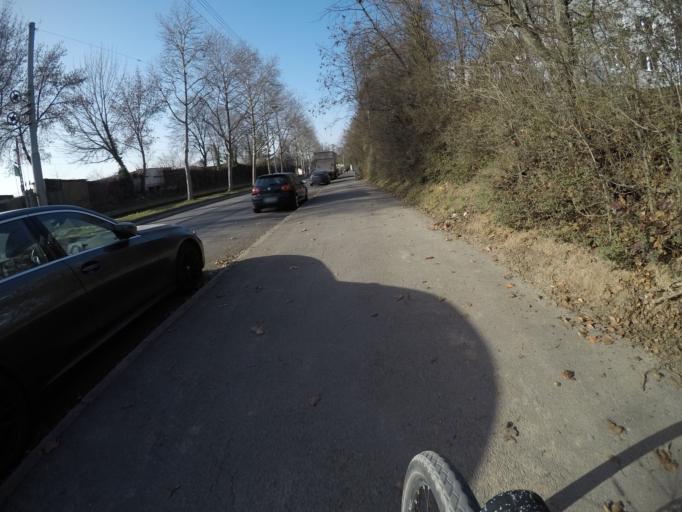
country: DE
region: Baden-Wuerttemberg
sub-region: Regierungsbezirk Stuttgart
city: Stuttgart-Ost
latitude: 48.7945
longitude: 9.2411
